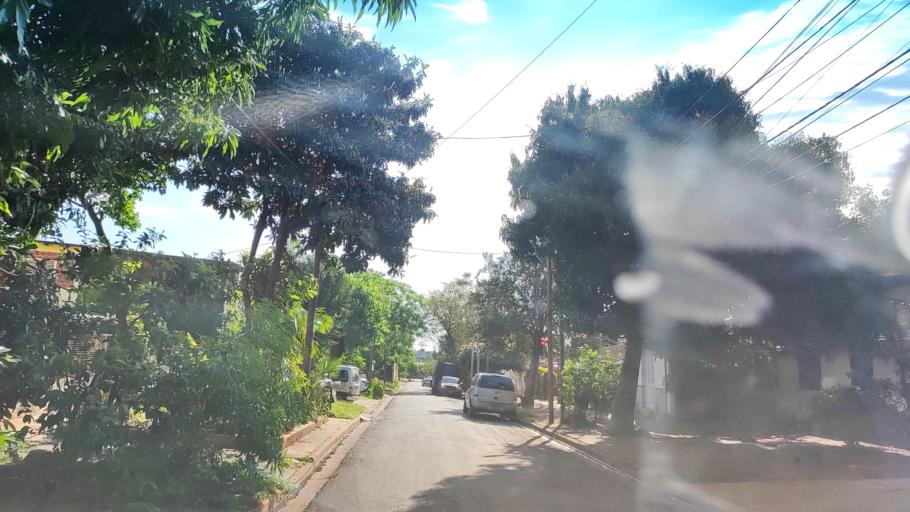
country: AR
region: Misiones
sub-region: Departamento de Capital
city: Posadas
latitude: -27.3768
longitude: -55.9275
